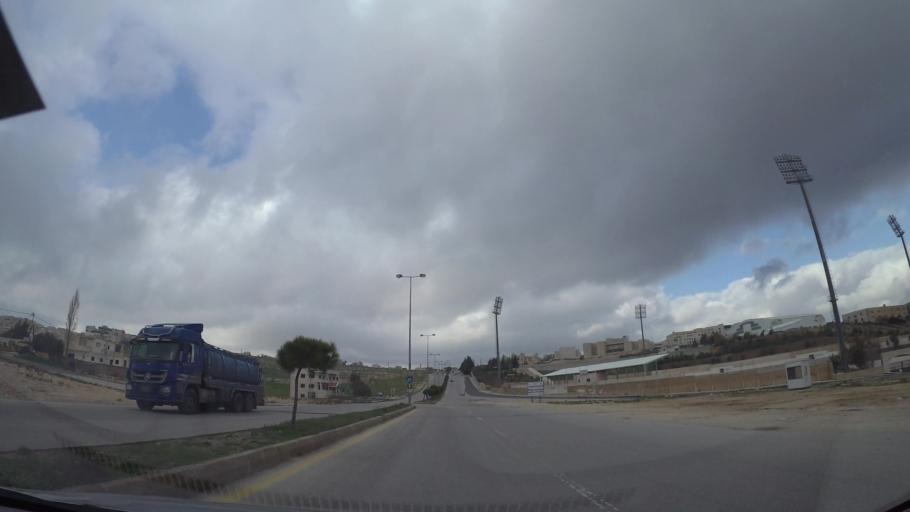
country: JO
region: Amman
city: Al Jubayhah
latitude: 32.0373
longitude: 35.8964
